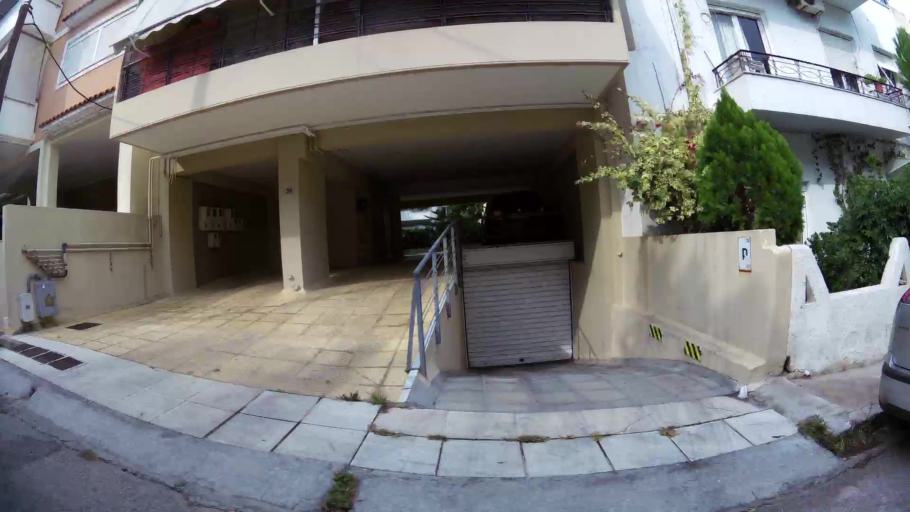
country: GR
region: Attica
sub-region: Nomarchia Athinas
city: Nea Ionia
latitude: 38.0324
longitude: 23.7647
